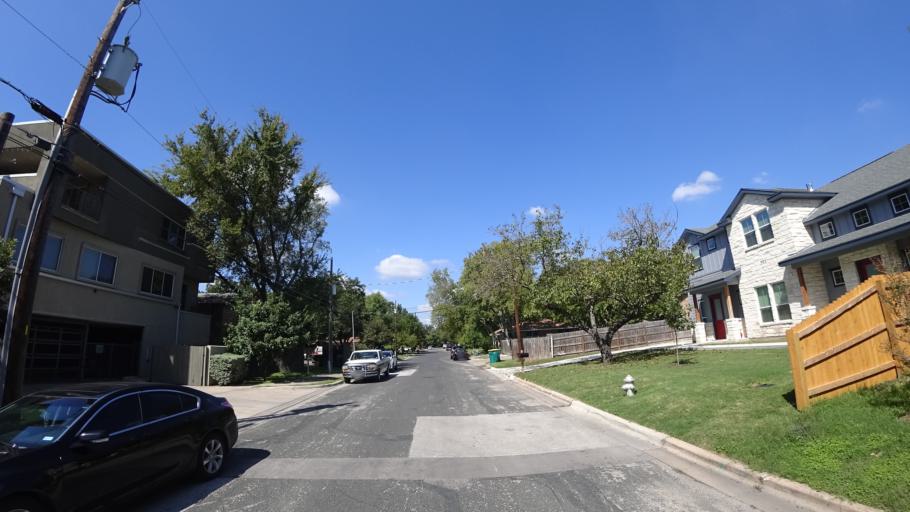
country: US
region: Texas
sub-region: Travis County
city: Austin
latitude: 30.3351
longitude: -97.7148
